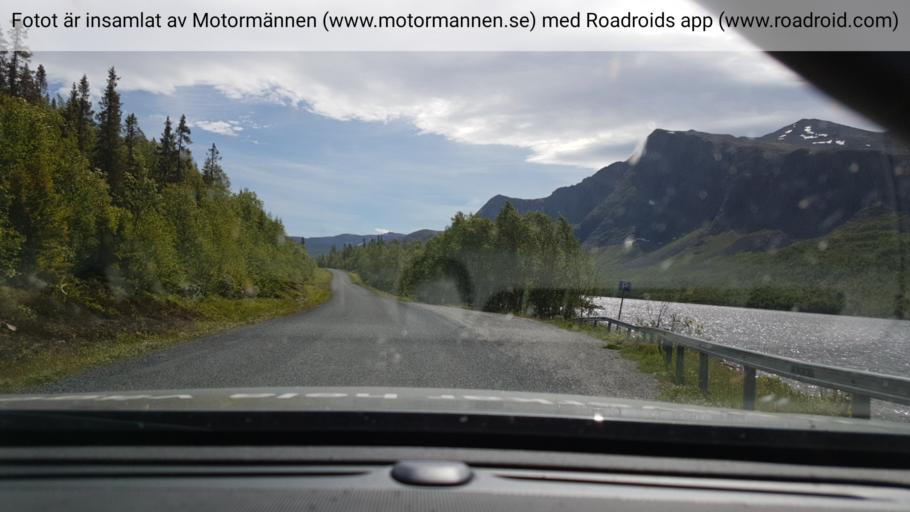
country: SE
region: Vaesterbotten
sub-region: Vilhelmina Kommun
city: Sjoberg
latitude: 65.2491
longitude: 15.4197
